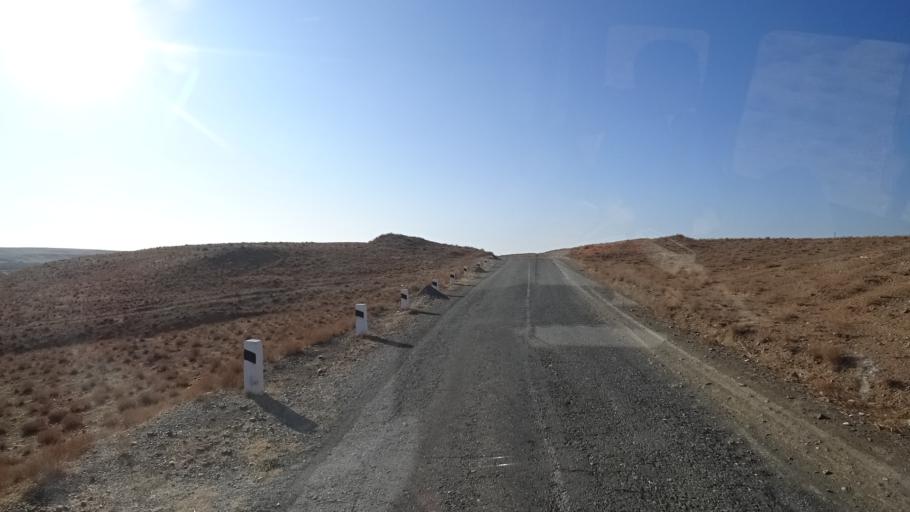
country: UZ
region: Navoiy
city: Beshrabot
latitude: 40.2585
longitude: 65.4743
